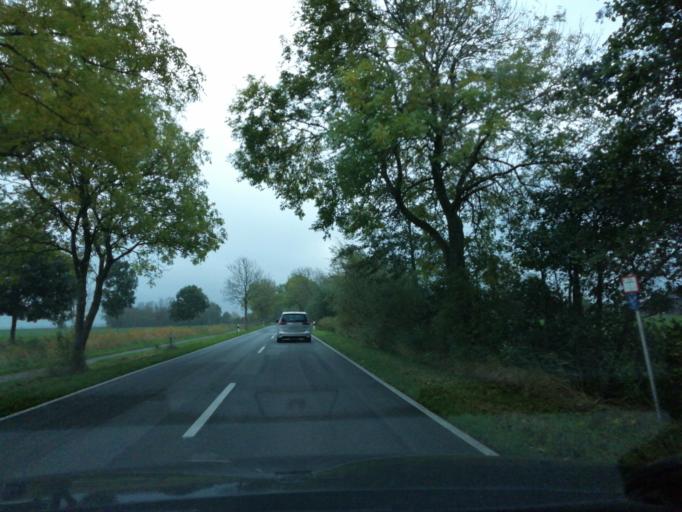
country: DE
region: Lower Saxony
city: Jever
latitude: 53.6813
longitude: 7.8617
